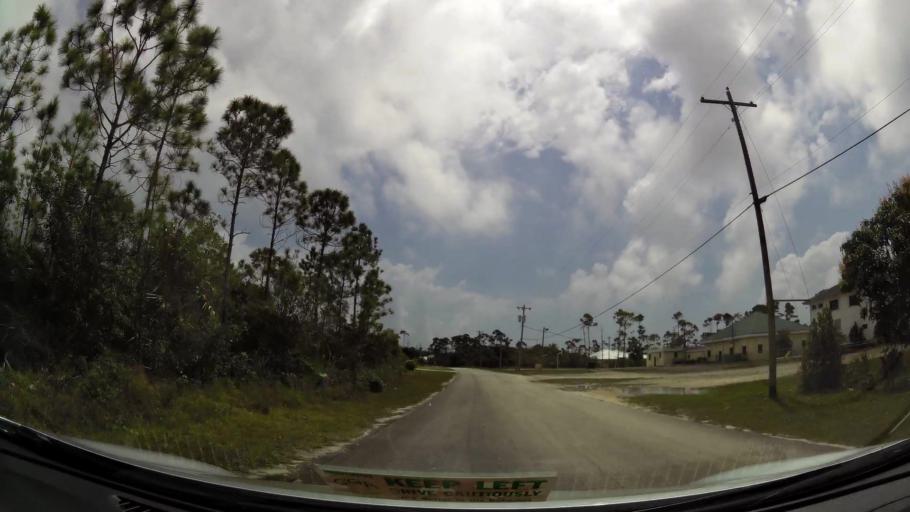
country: BS
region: Freeport
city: Lucaya
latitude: 26.5249
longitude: -78.6532
